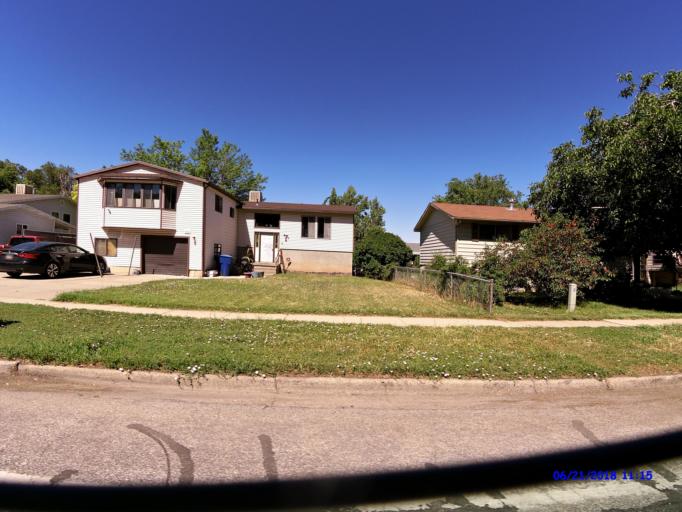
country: US
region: Utah
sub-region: Weber County
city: Harrisville
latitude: 41.2676
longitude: -111.9593
